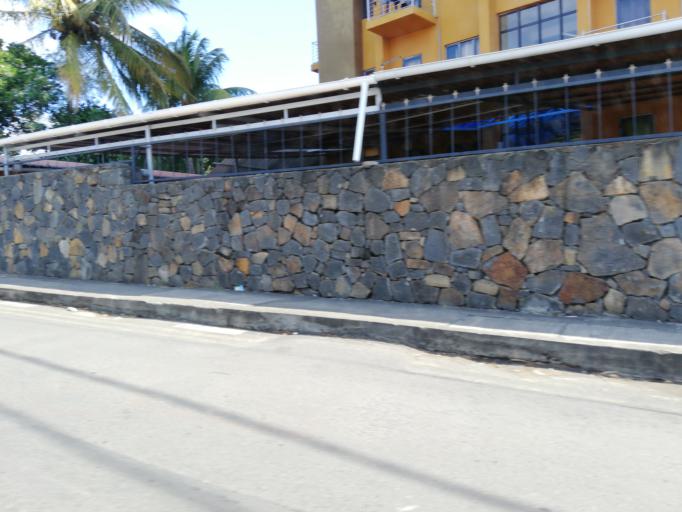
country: MU
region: Port Louis
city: Port Louis
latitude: -20.1647
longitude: 57.4798
